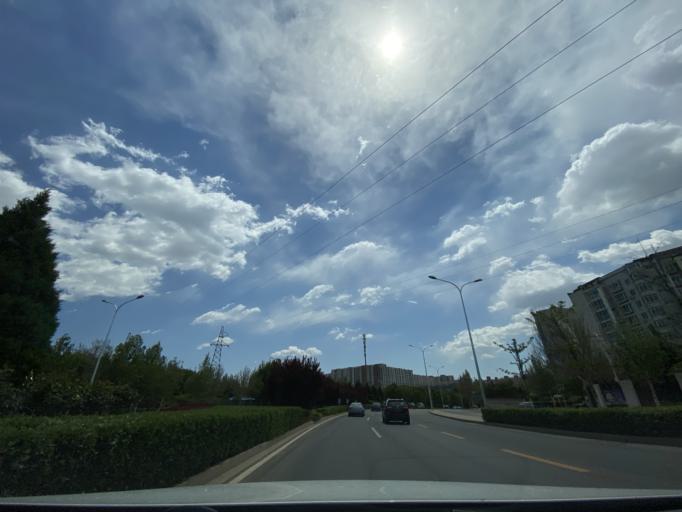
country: CN
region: Beijing
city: Sijiqing
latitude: 39.9336
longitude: 116.2460
